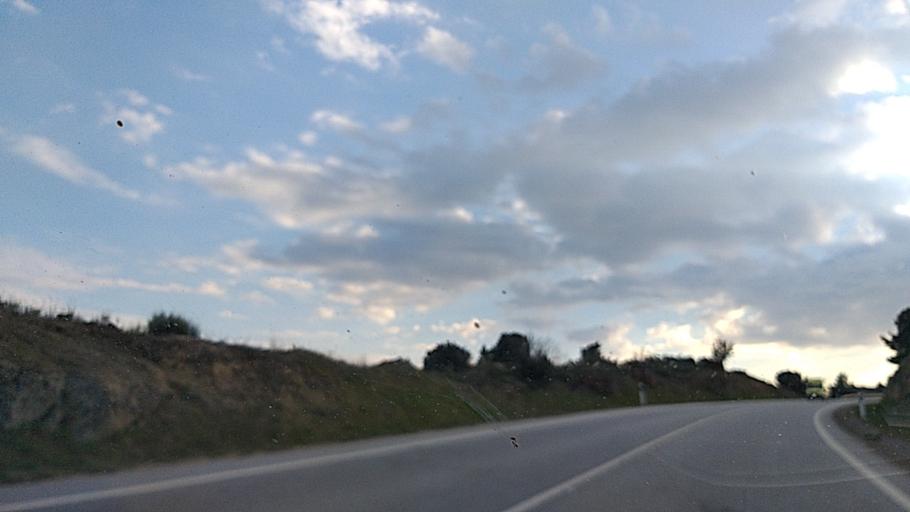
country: ES
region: Castille and Leon
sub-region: Provincia de Salamanca
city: Aldea del Obispo
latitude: 40.6886
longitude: -6.9422
